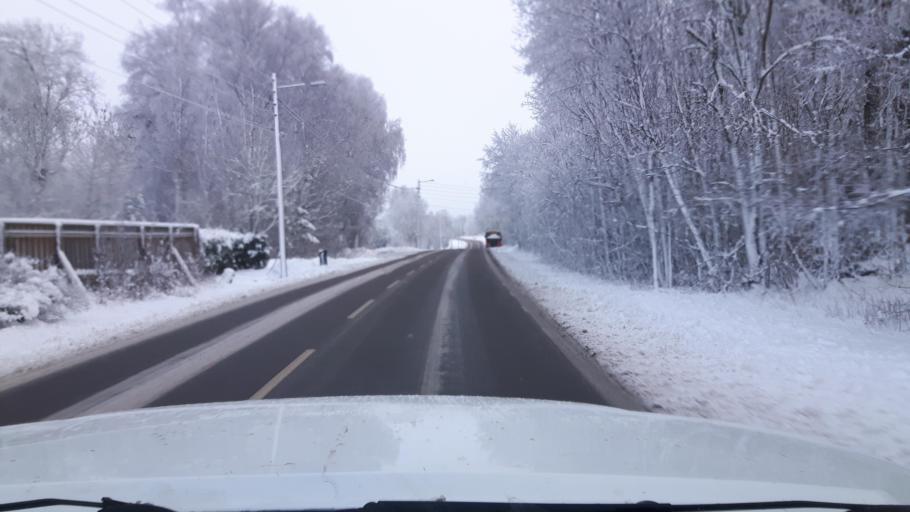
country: SE
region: Halland
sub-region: Kungsbacka Kommun
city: Onsala
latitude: 57.4101
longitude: 11.9964
